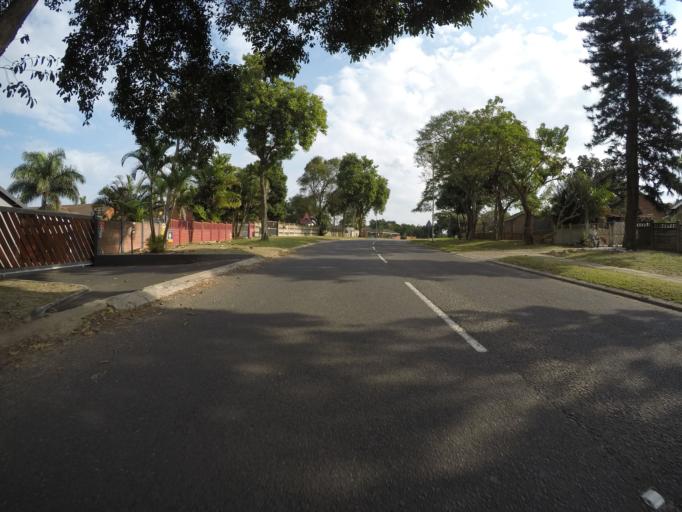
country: ZA
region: KwaZulu-Natal
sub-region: uThungulu District Municipality
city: Richards Bay
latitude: -28.7413
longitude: 32.0636
